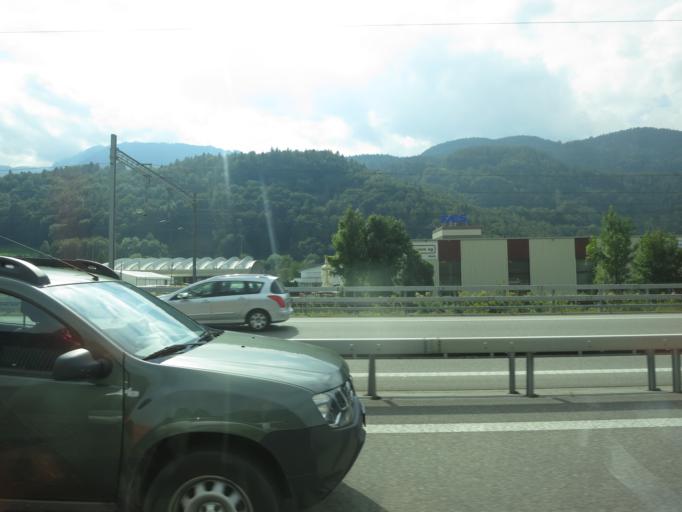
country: CH
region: Saint Gallen
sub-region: Wahlkreis Sarganserland
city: Sargans
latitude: 47.0559
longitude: 9.4138
